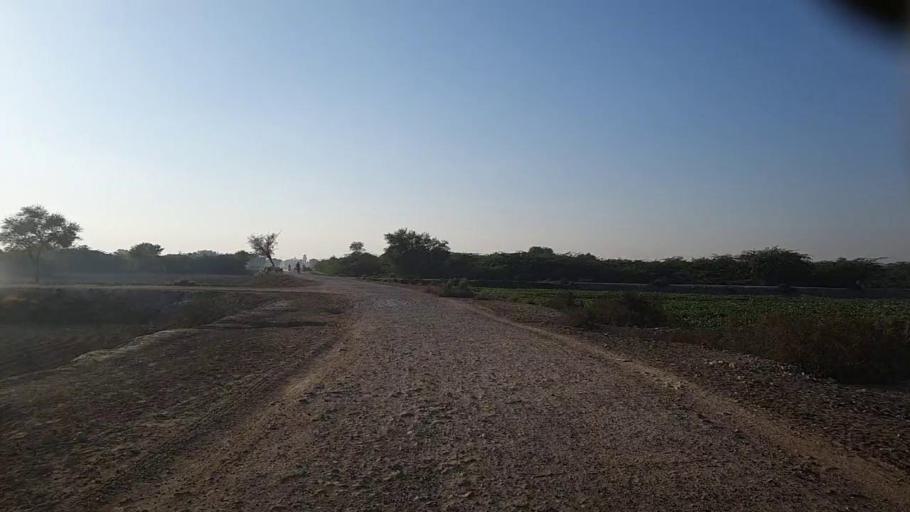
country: PK
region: Sindh
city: Pad Idan
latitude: 26.7345
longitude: 68.3439
